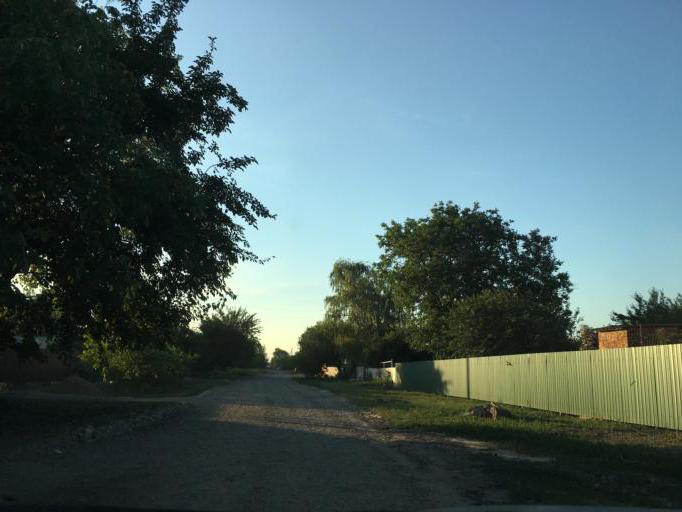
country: RU
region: Krasnodarskiy
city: Kushchevskaya
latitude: 46.5658
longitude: 39.6496
